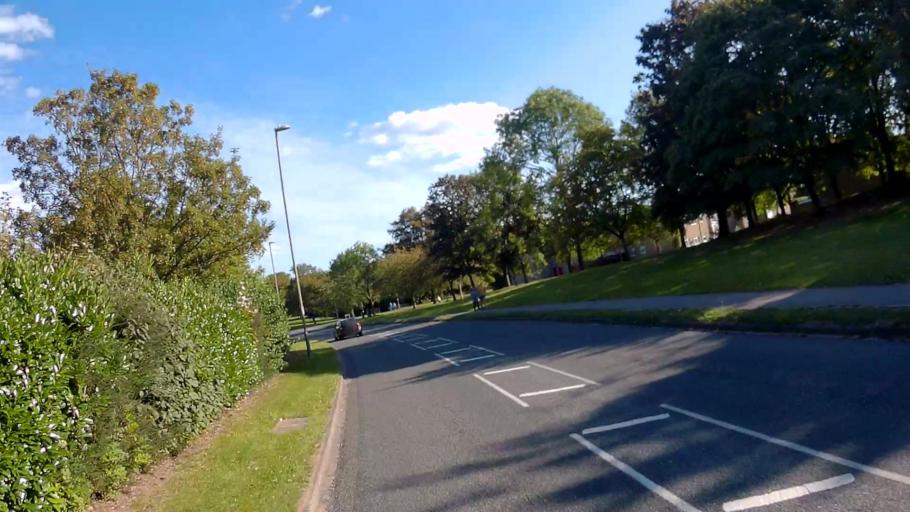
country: GB
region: England
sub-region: Hampshire
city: Basingstoke
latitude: 51.2424
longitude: -1.1173
